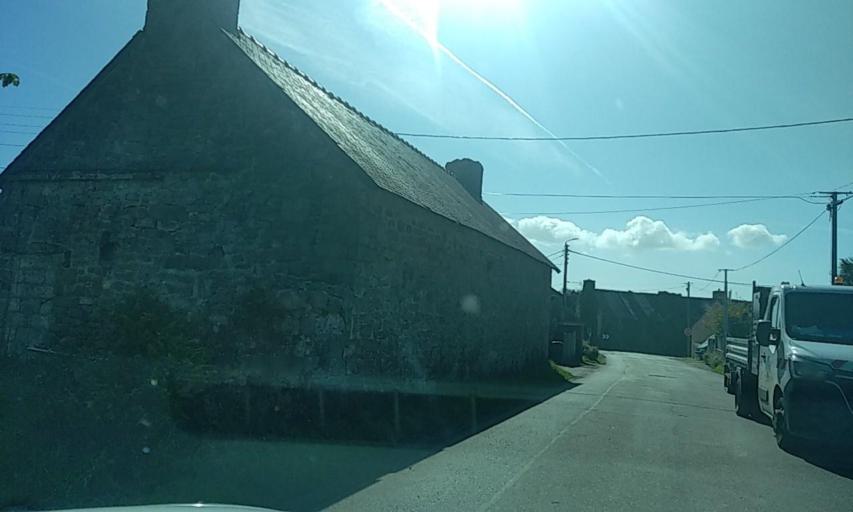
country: FR
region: Brittany
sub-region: Departement du Morbihan
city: Ploemeur
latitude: 47.7159
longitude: -3.4541
